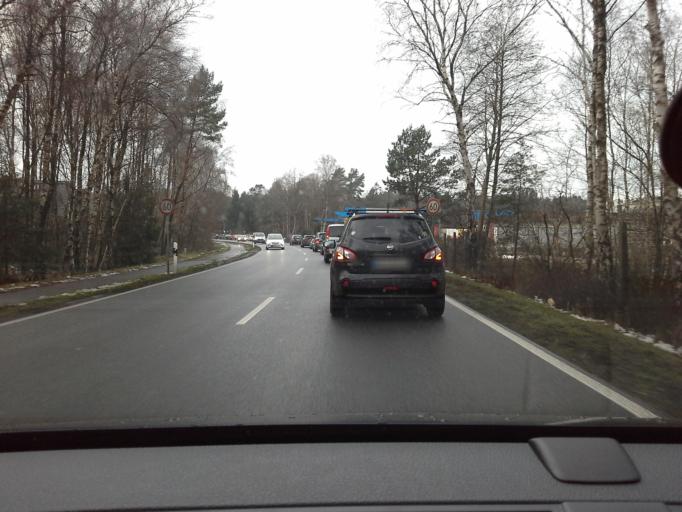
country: DE
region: Schleswig-Holstein
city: Henstedt-Ulzburg
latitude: 53.7482
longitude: 9.9996
